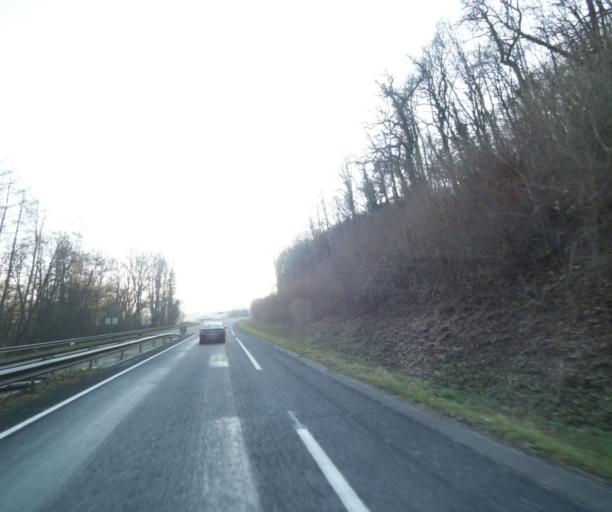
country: FR
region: Champagne-Ardenne
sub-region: Departement de la Haute-Marne
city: Chevillon
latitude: 48.5347
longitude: 5.0978
